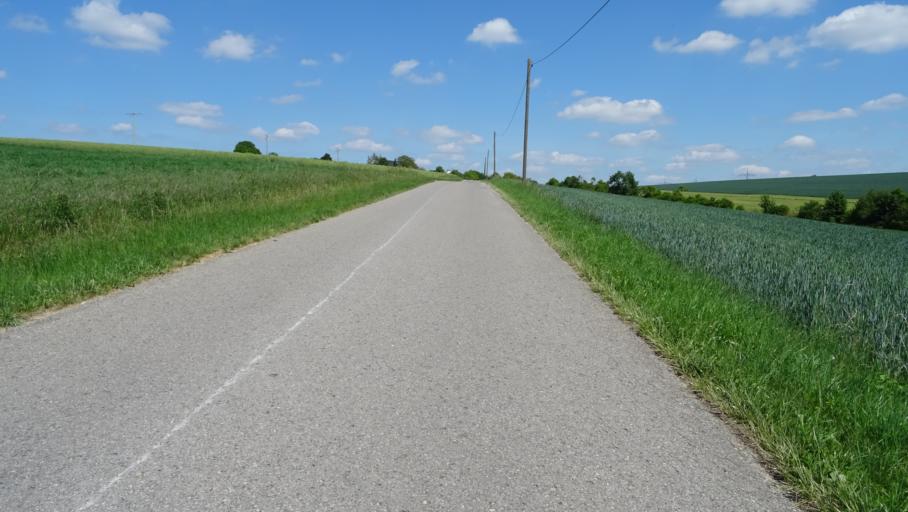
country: DE
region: Baden-Wuerttemberg
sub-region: Karlsruhe Region
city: Buchen
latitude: 49.5020
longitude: 9.3329
